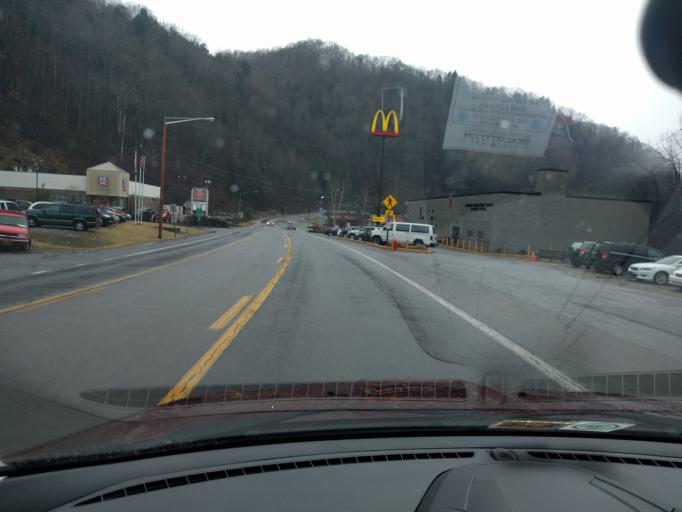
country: US
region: West Virginia
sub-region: McDowell County
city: Welch
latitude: 37.4320
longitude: -81.5684
